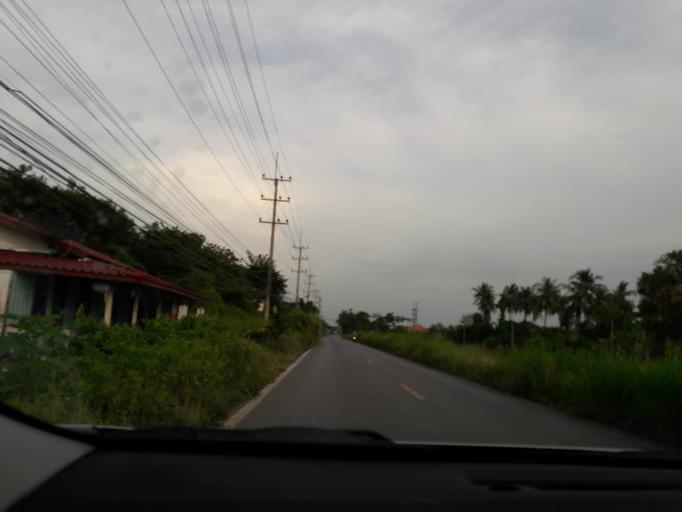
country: TH
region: Ang Thong
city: Ang Thong
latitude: 14.5861
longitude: 100.4606
